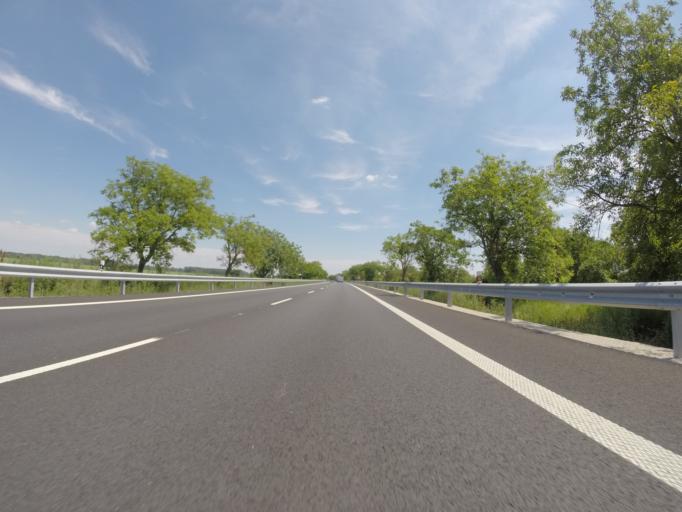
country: SK
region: Trnavsky
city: Sladkovicovo
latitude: 48.1990
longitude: 17.5658
